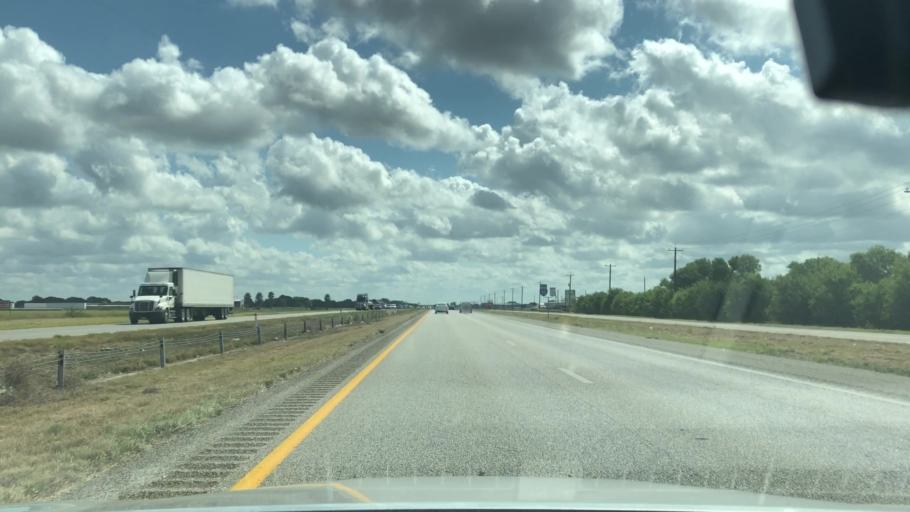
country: US
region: Texas
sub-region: Guadalupe County
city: Marion
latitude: 29.5100
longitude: -98.1626
